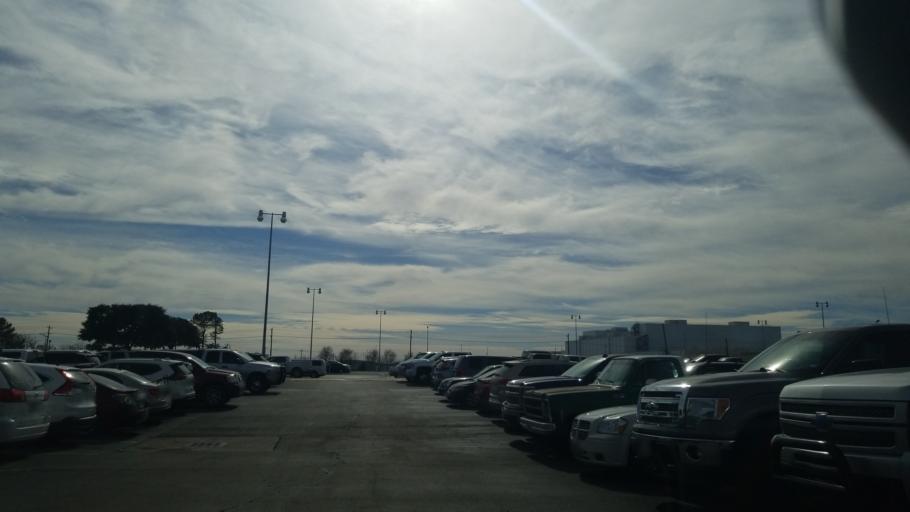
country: US
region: Texas
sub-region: Denton County
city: Denton
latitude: 33.2034
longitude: -97.1780
